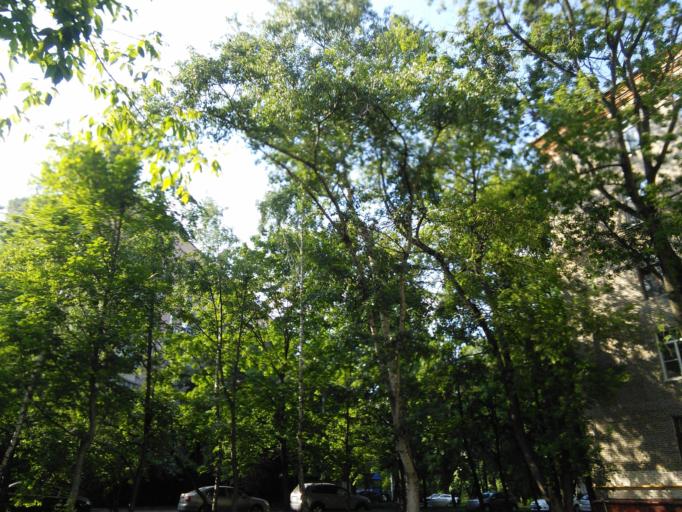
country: RU
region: Moskovskaya
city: Bogorodskoye
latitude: 55.8133
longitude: 37.7168
